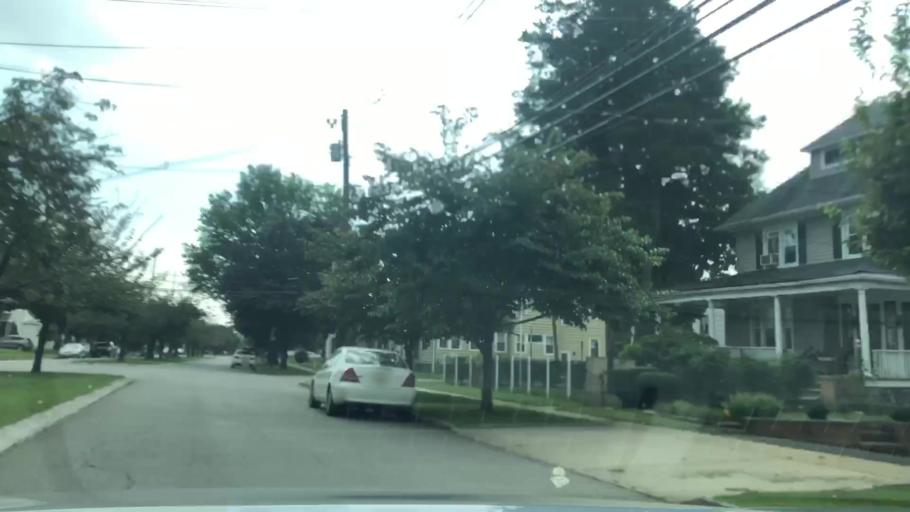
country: US
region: New Jersey
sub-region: Essex County
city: Bloomfield
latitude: 40.7881
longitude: -74.1847
